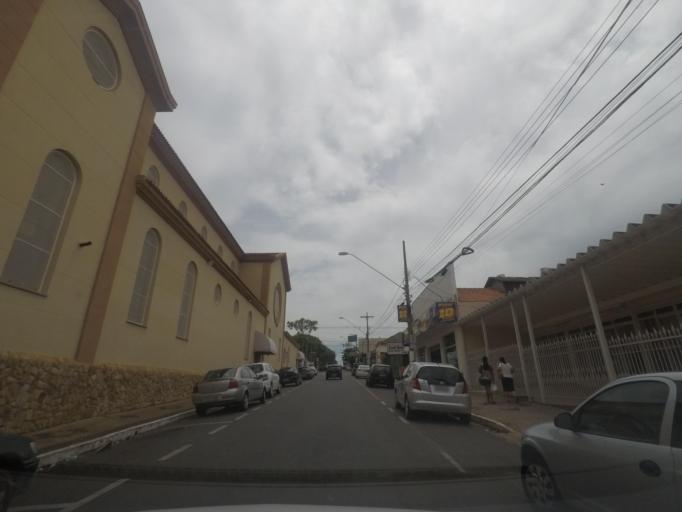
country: BR
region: Sao Paulo
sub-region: Sumare
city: Sumare
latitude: -22.8222
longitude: -47.2674
